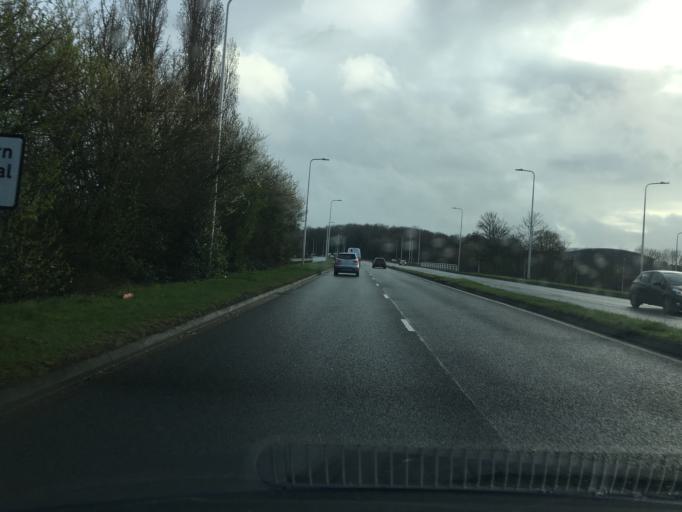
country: GB
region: England
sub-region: Bracknell Forest
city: Bracknell
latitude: 51.4090
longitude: -0.7665
